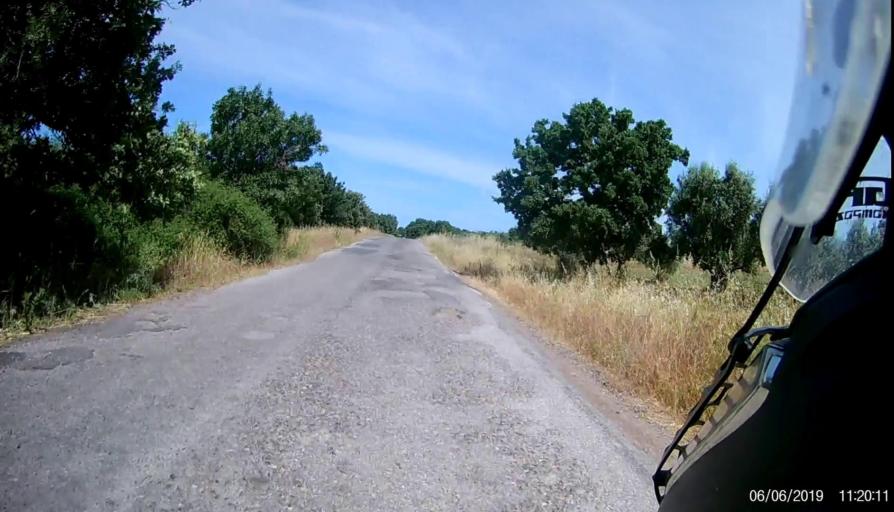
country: TR
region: Canakkale
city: Gulpinar
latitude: 39.6637
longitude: 26.1638
